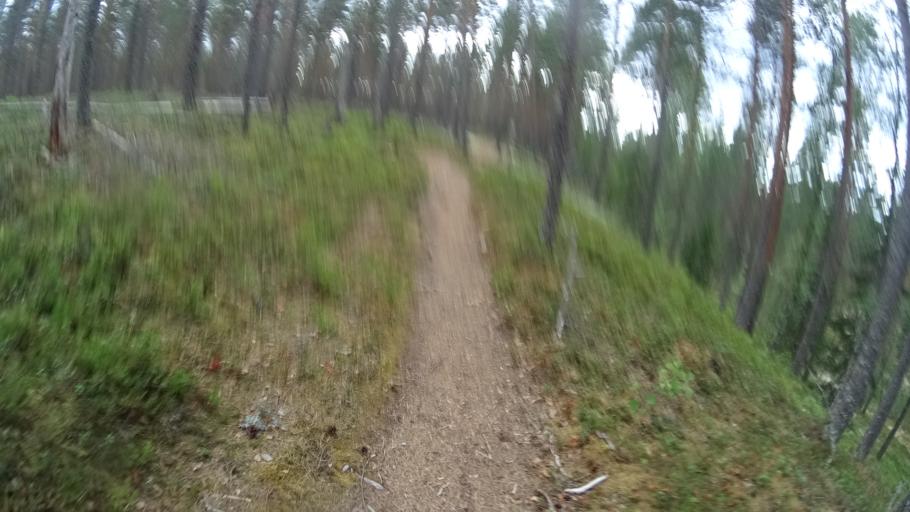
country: FI
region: Satakunta
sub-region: Pohjois-Satakunta
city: Jaemijaervi
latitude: 61.7698
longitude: 22.7762
